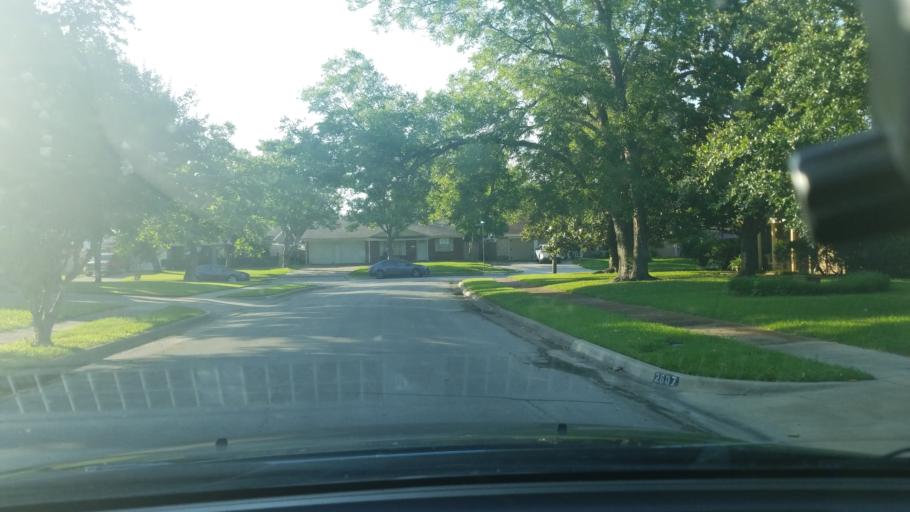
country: US
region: Texas
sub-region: Dallas County
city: Mesquite
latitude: 32.8026
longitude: -96.6410
